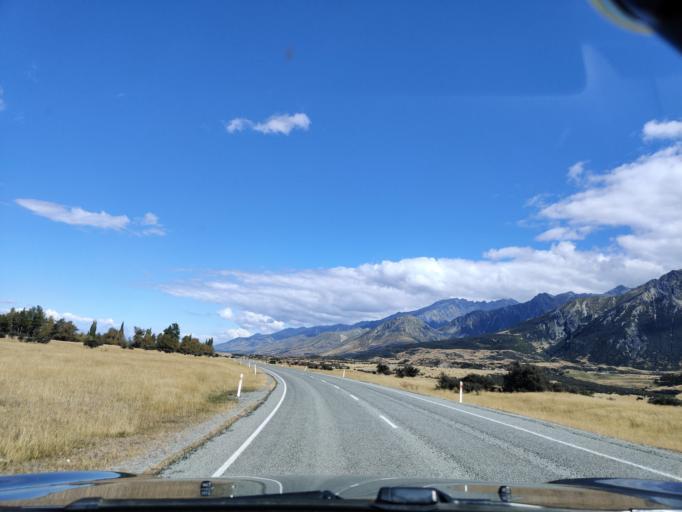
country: NZ
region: Canterbury
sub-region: Timaru District
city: Pleasant Point
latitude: -43.7869
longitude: 170.1195
